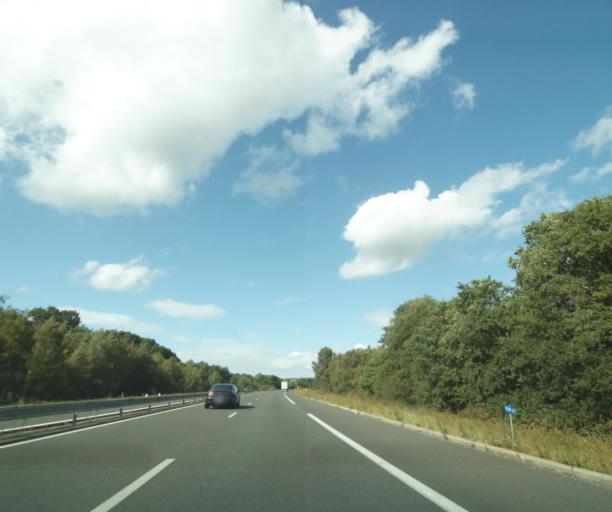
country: FR
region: Centre
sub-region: Departement du Loiret
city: Jouy-le-Potier
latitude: 47.7844
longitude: 1.8464
